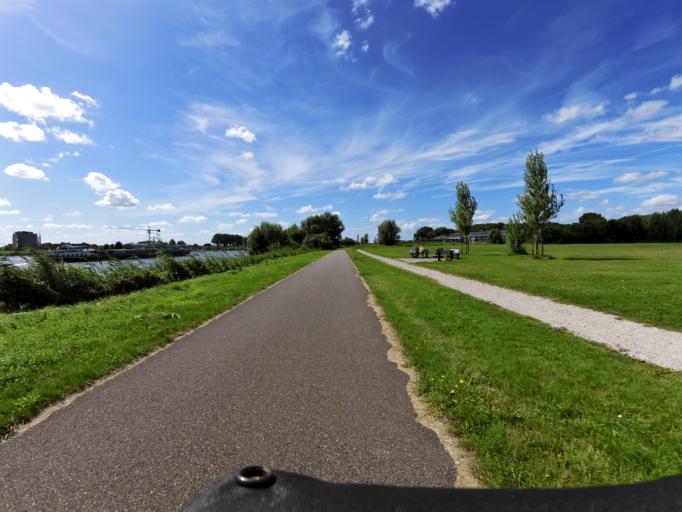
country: NL
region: South Holland
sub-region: Gemeente Zwijndrecht
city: Heerjansdam
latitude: 51.8086
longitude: 4.5855
